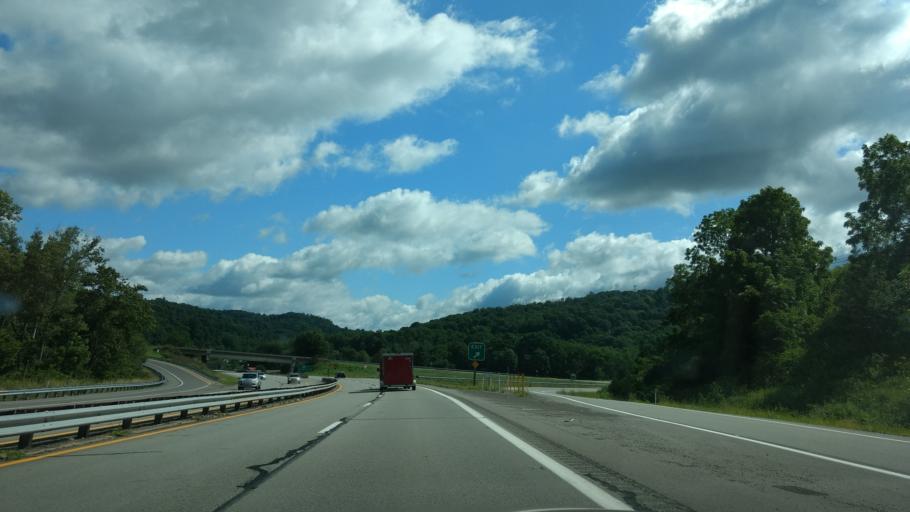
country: US
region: Pennsylvania
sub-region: Allegheny County
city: Plum
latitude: 40.5006
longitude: -79.6803
